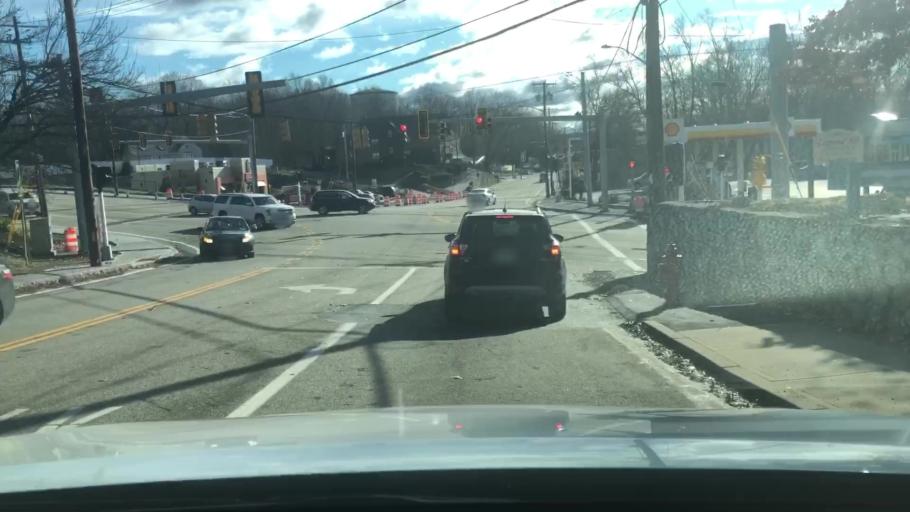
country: US
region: Rhode Island
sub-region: Providence County
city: Woonsocket
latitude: 42.0160
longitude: -71.4823
